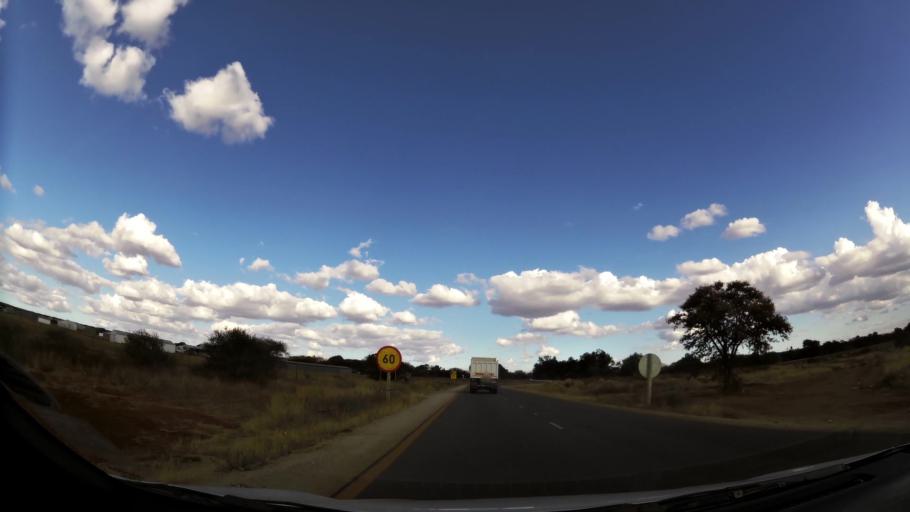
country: ZA
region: Limpopo
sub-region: Capricorn District Municipality
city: Polokwane
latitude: -23.9314
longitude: 29.4715
